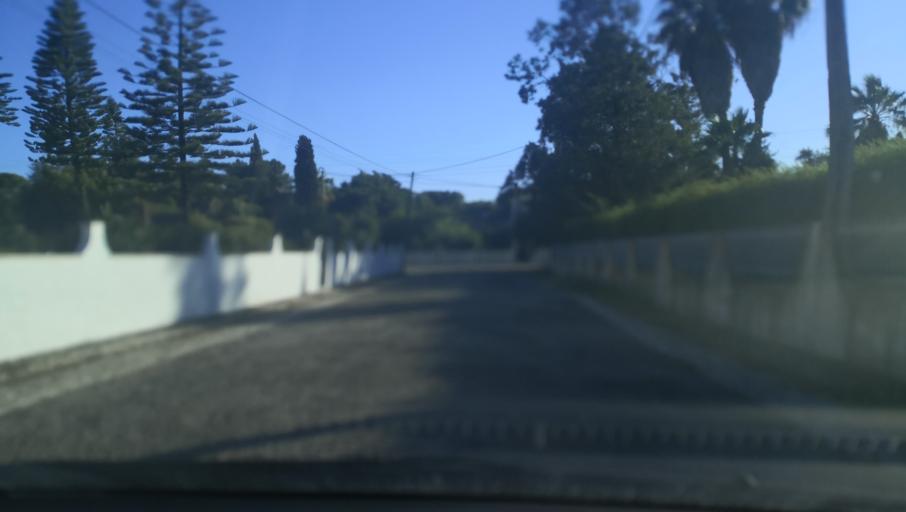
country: PT
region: Setubal
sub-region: Palmela
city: Palmela
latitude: 38.5537
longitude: -8.8896
